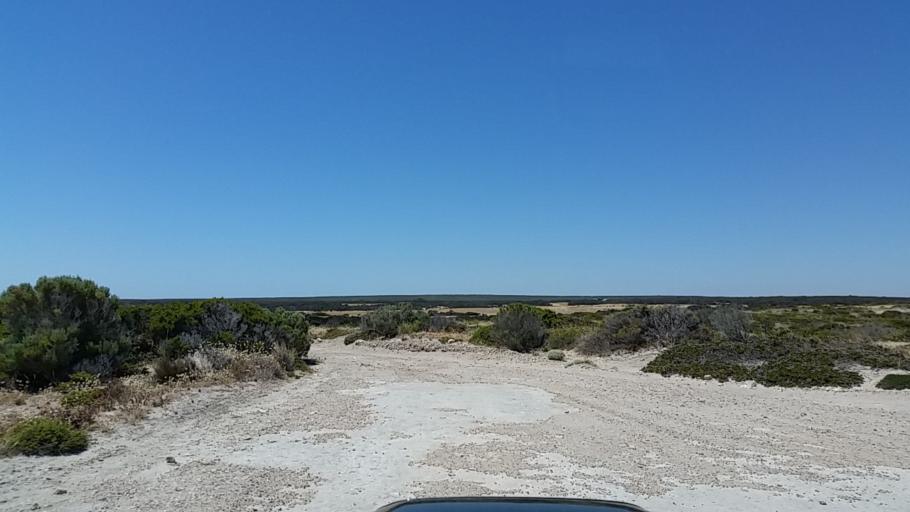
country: AU
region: South Australia
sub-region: Yorke Peninsula
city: Honiton
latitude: -35.2277
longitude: 137.0695
